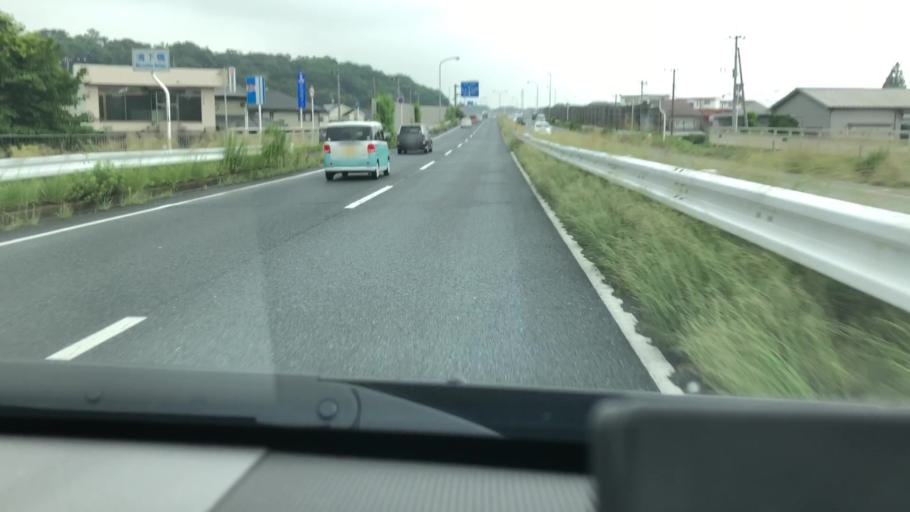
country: JP
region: Chiba
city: Kisarazu
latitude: 35.4411
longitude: 139.9715
